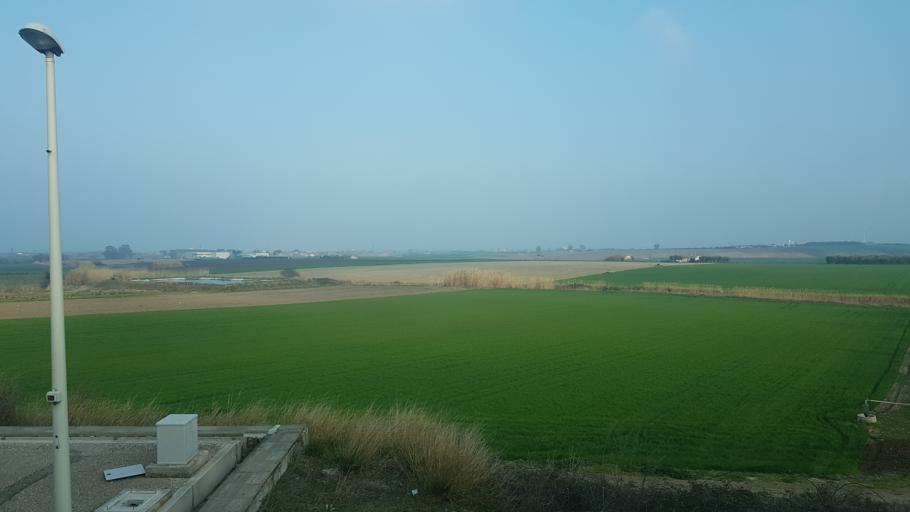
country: IT
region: Apulia
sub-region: Provincia di Foggia
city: Lesina
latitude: 41.8504
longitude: 15.2959
